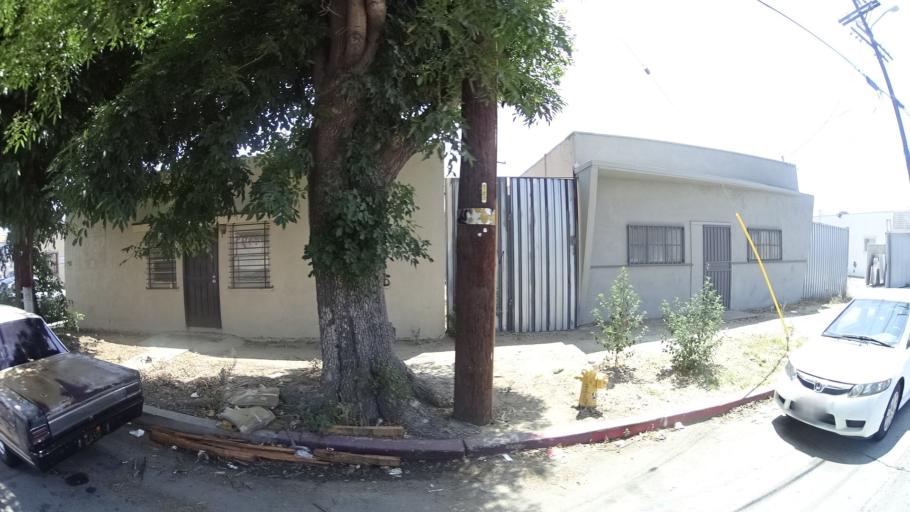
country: US
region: California
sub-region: Los Angeles County
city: Van Nuys
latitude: 34.2055
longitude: -118.4247
